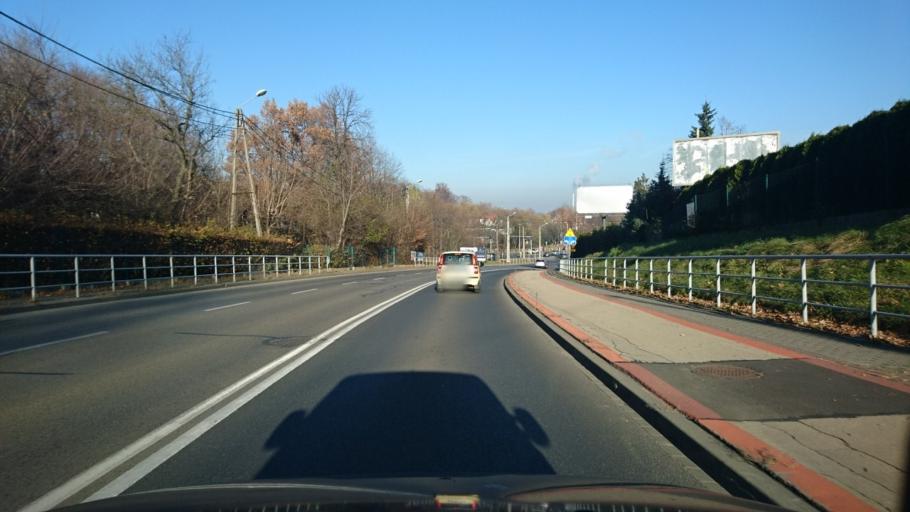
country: PL
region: Silesian Voivodeship
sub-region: Bielsko-Biala
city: Bielsko-Biala
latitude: 49.7997
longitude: 19.0414
